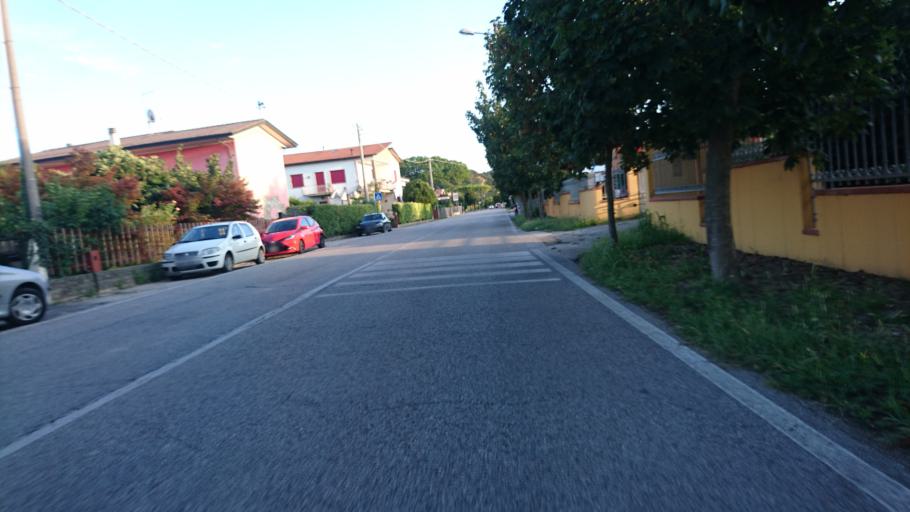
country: IT
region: Veneto
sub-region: Provincia di Padova
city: Montegrotto Terme
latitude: 45.3393
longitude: 11.7764
